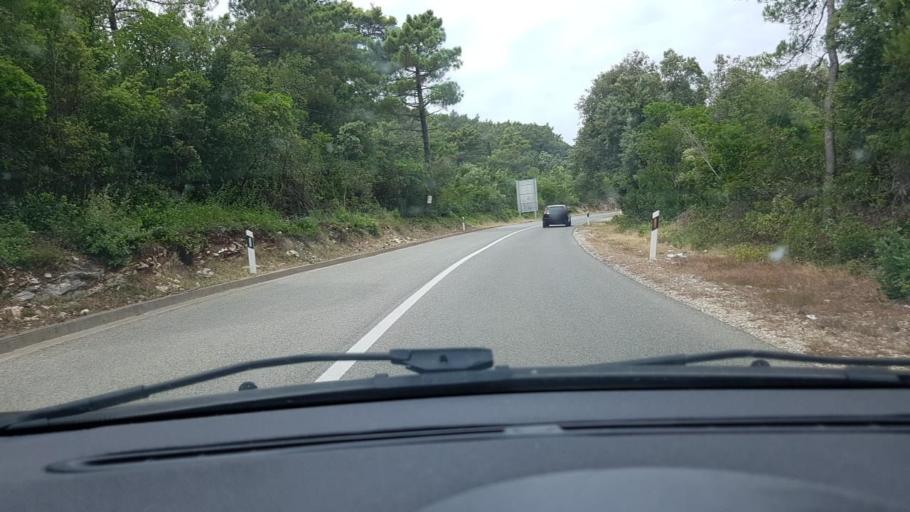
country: HR
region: Dubrovacko-Neretvanska
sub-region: Grad Korcula
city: Zrnovo
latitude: 42.9353
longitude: 17.1010
